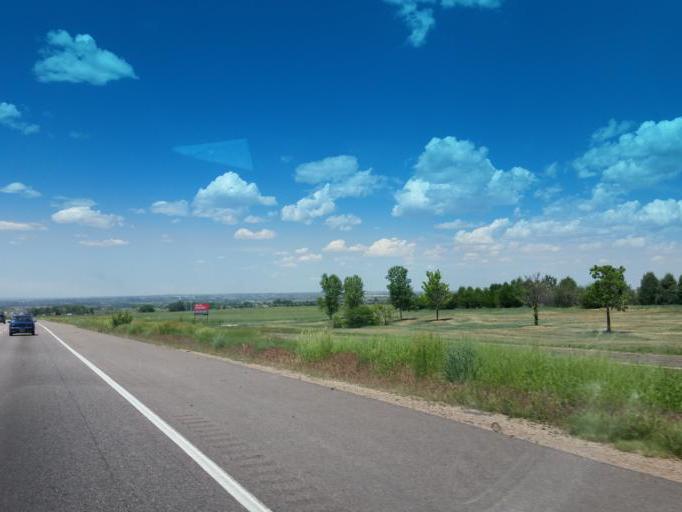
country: US
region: Colorado
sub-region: Weld County
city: Windsor
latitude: 40.4491
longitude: -104.9919
